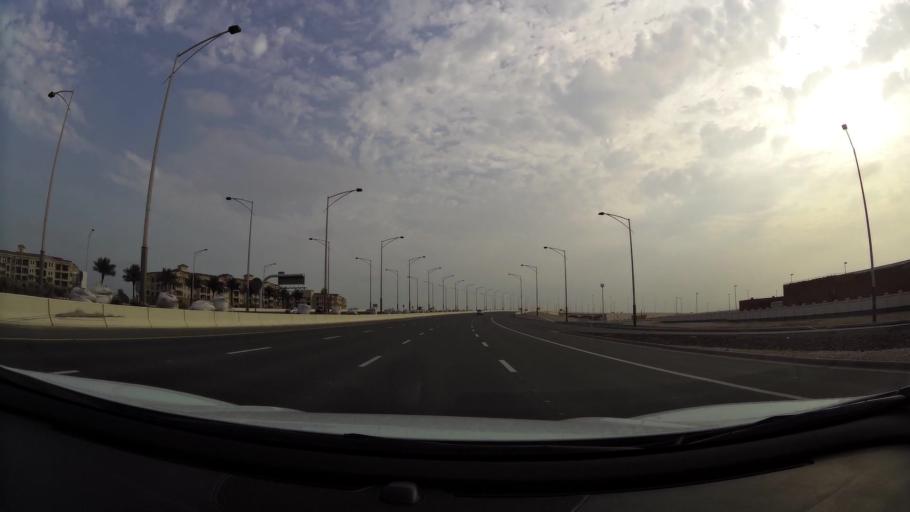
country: AE
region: Abu Dhabi
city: Abu Dhabi
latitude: 24.5476
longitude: 54.4518
